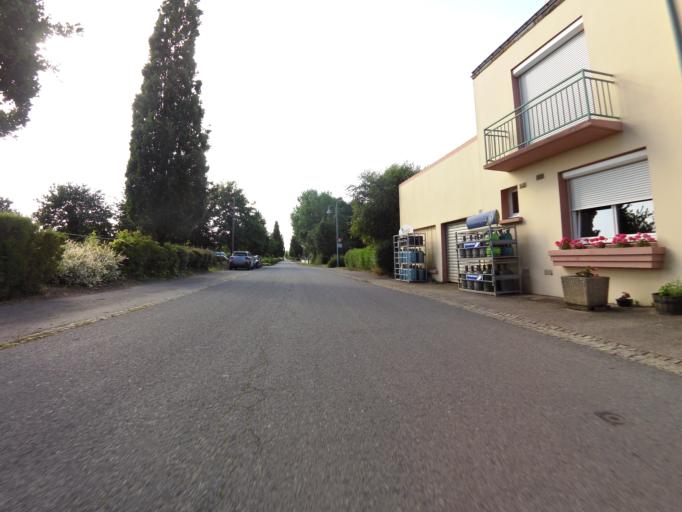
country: FR
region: Brittany
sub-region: Departement du Morbihan
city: Pluherlin
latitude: 47.6969
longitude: -2.3644
